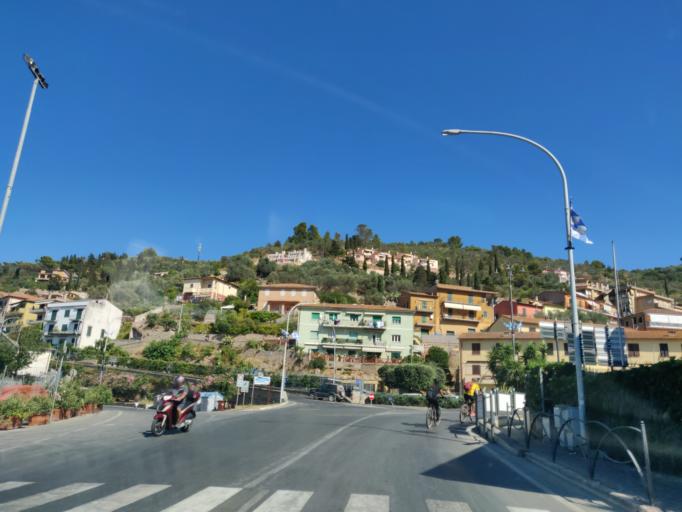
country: IT
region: Tuscany
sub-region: Provincia di Grosseto
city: Monte Argentario
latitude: 42.4344
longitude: 11.1233
